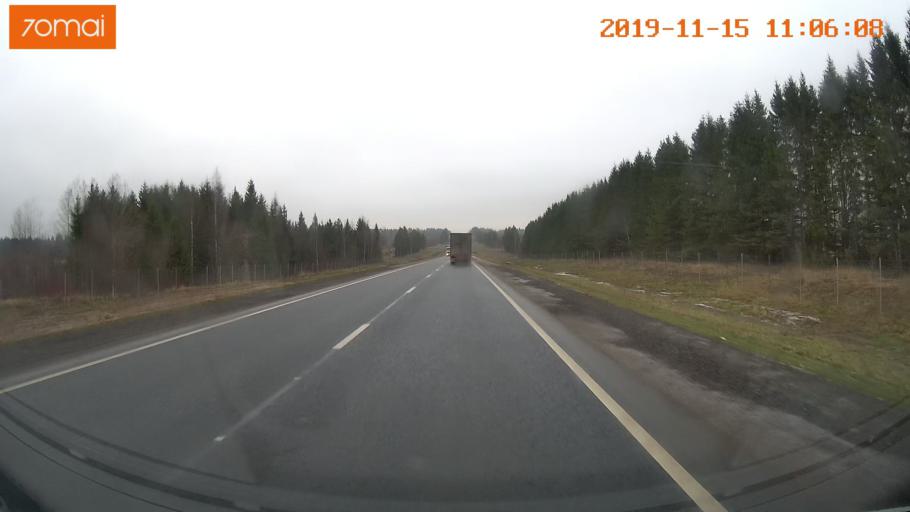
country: RU
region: Vologda
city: Chebsara
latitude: 59.1189
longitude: 39.0199
